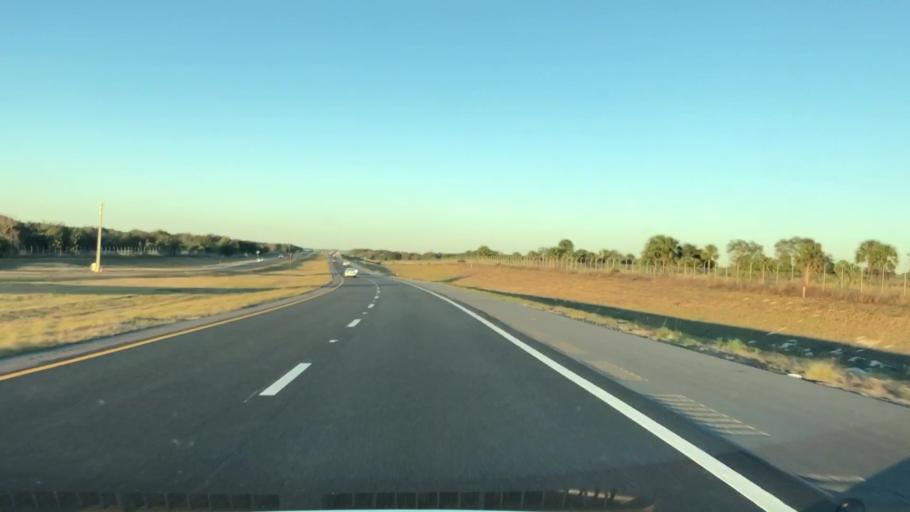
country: US
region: Florida
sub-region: Lake County
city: Mount Plymouth
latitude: 28.7823
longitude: -81.5216
